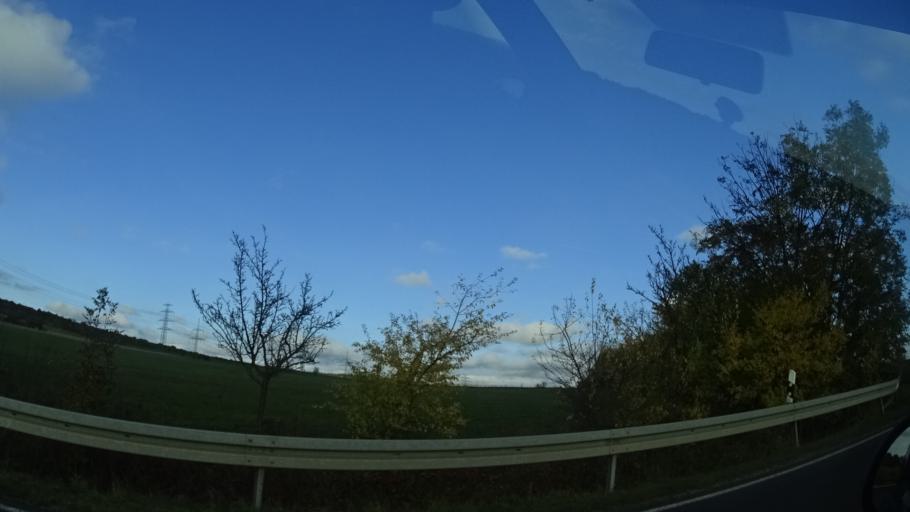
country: DE
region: Thuringia
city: Elleben
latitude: 50.8783
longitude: 11.0963
